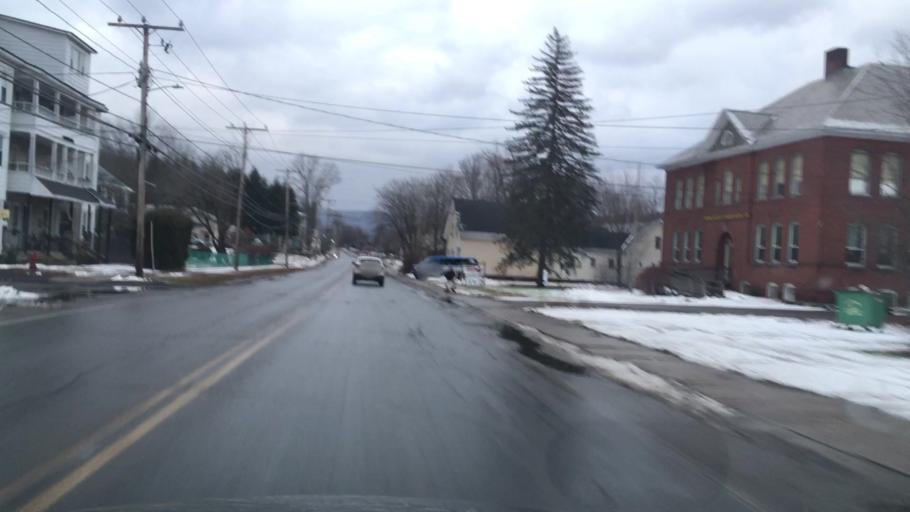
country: US
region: New Hampshire
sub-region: Sullivan County
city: Claremont
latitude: 43.3785
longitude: -72.3428
